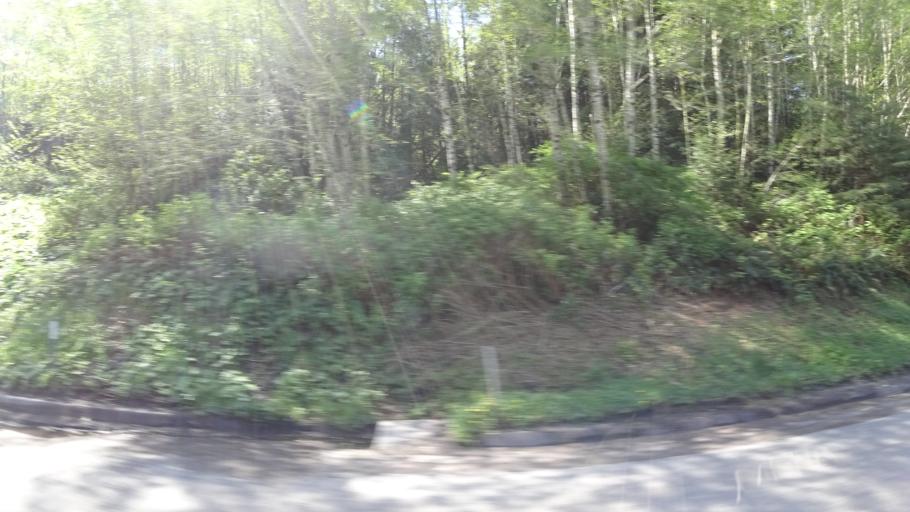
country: US
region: California
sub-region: Del Norte County
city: Bertsch-Oceanview
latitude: 41.4249
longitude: -124.0060
